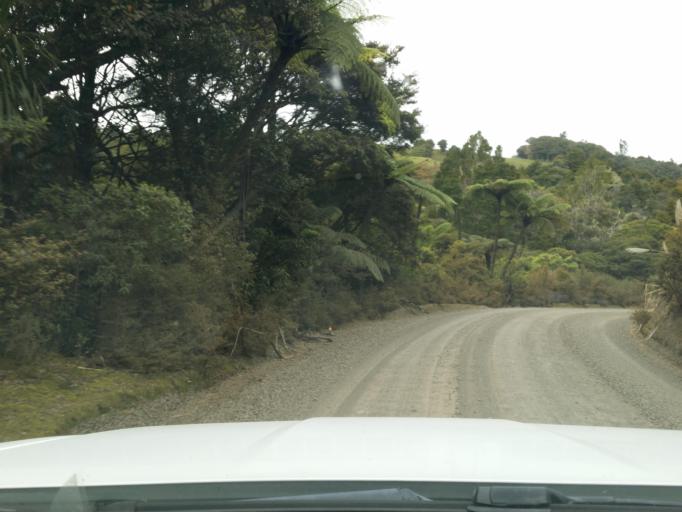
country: NZ
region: Northland
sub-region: Kaipara District
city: Dargaville
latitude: -35.7116
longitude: 173.6333
